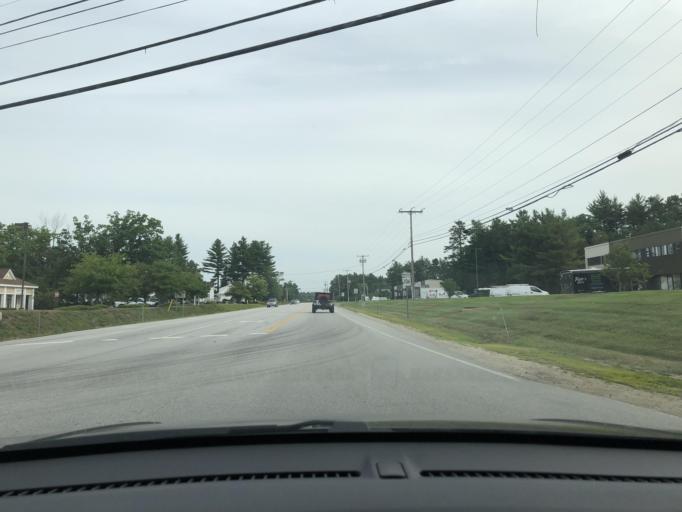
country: US
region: New Hampshire
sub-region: Merrimack County
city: Concord
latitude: 43.2132
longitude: -71.4833
